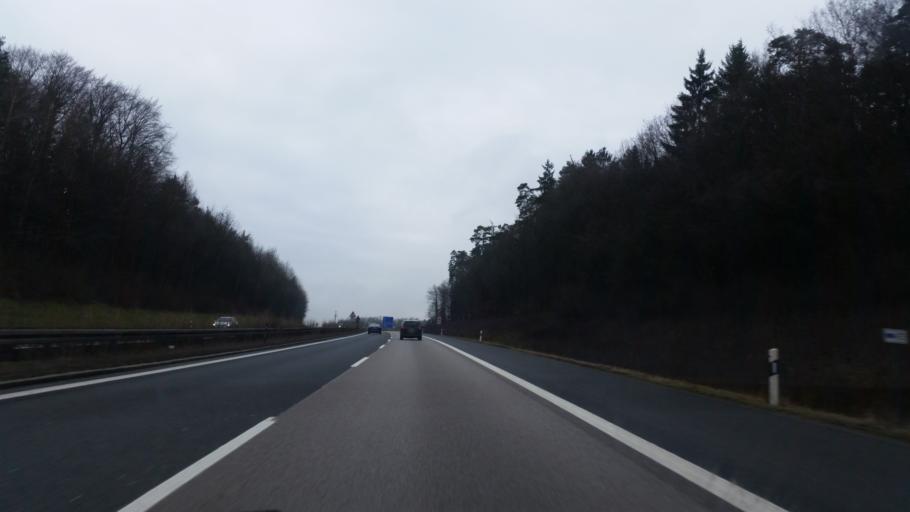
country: DE
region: Bavaria
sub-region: Regierungsbezirk Mittelfranken
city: Herrieden
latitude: 49.2643
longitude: 10.5169
